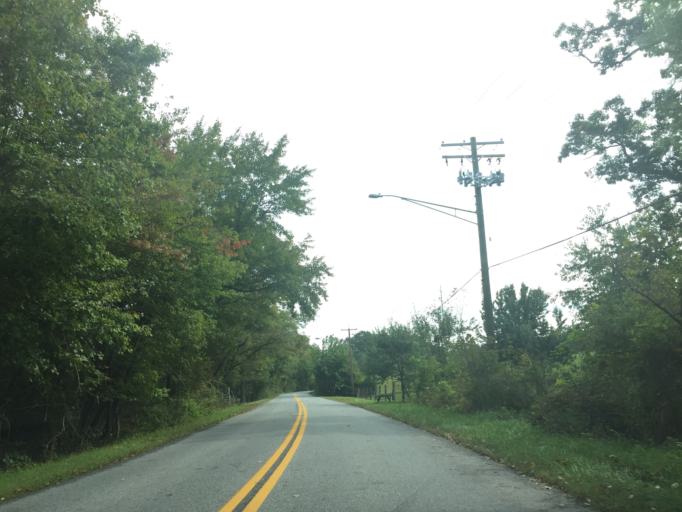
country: US
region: Maryland
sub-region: Baltimore County
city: White Marsh
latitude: 39.3634
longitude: -76.4402
